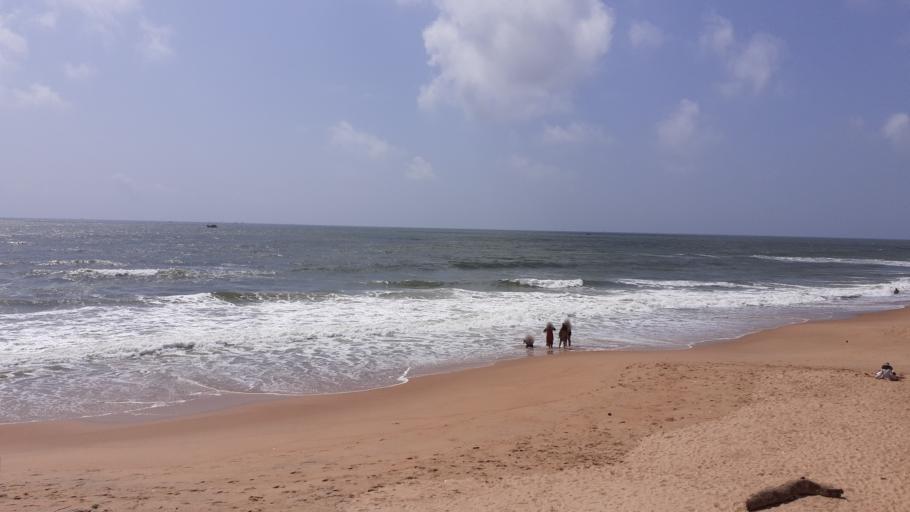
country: IN
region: Goa
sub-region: North Goa
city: Candolim
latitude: 15.5005
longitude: 73.7677
